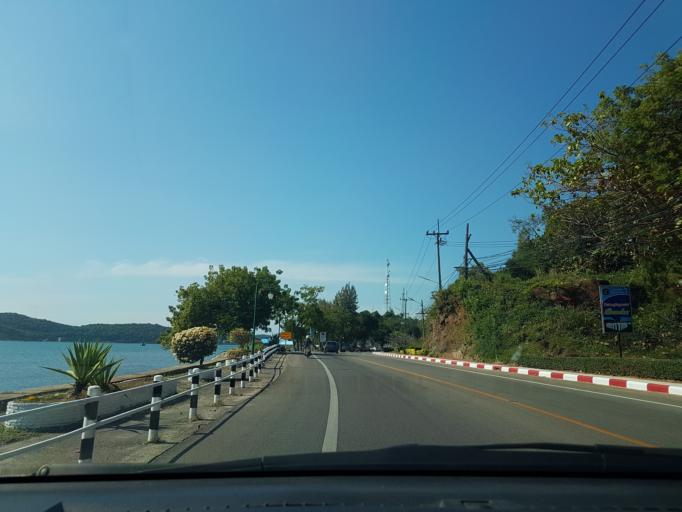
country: TH
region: Chon Buri
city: Sattahip
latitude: 12.6600
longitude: 100.8915
